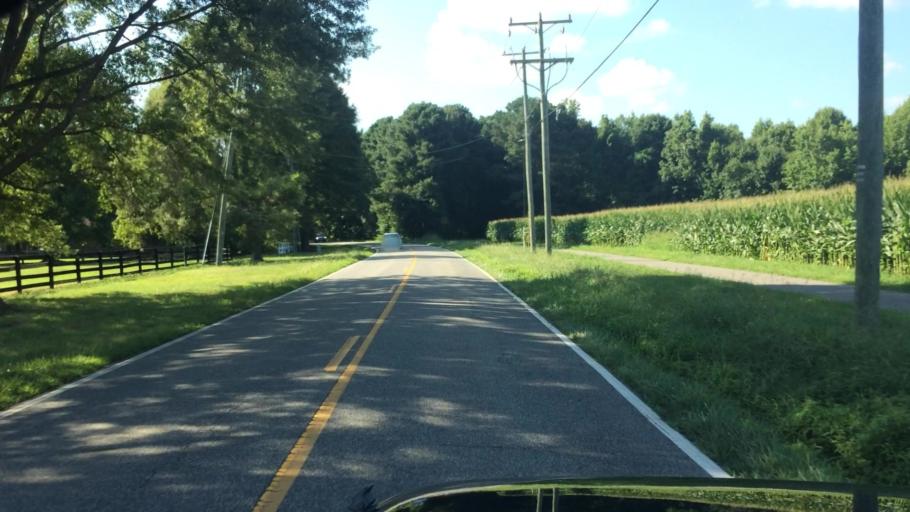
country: US
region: Virginia
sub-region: James City County
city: Williamsburg
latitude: 37.2366
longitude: -76.7860
